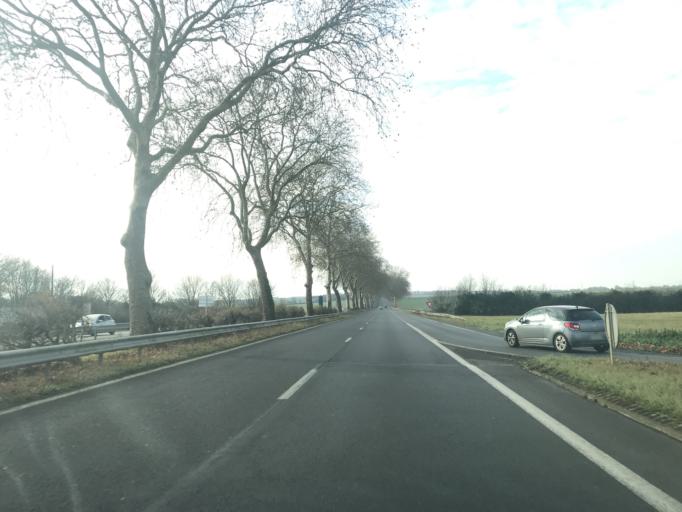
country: FR
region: Poitou-Charentes
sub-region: Departement des Deux-Sevres
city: Chauray
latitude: 46.3499
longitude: -0.3434
